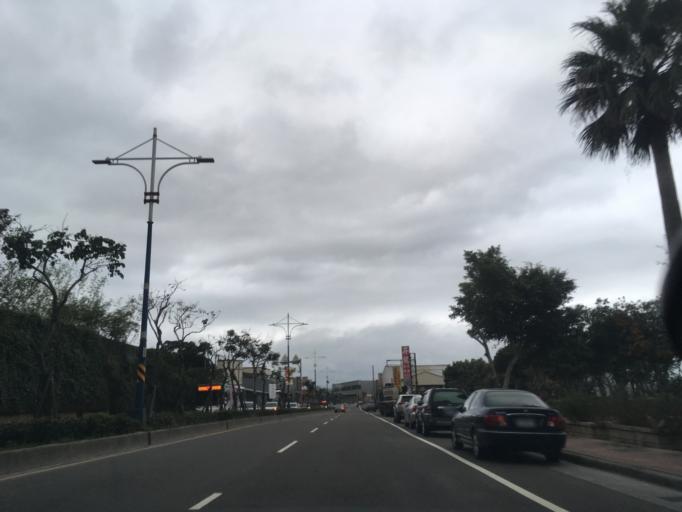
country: TW
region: Taipei
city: Taipei
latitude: 25.1514
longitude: 121.4423
